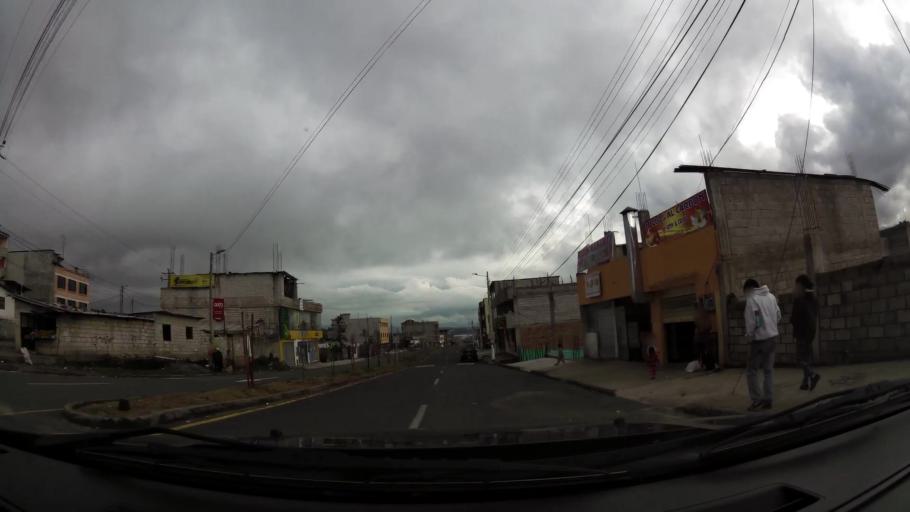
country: EC
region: Pichincha
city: Sangolqui
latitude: -0.3097
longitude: -78.5262
